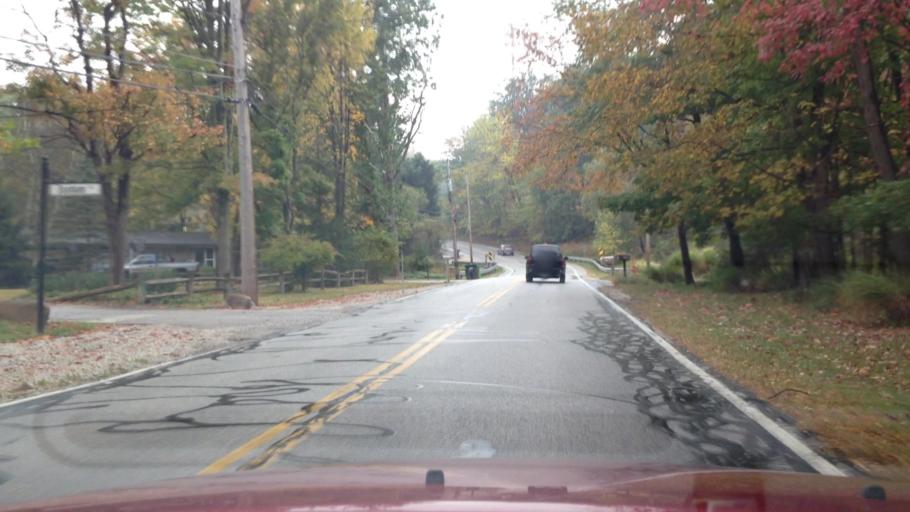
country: US
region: Ohio
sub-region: Cuyahoga County
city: Walton Hills
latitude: 41.3560
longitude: -81.5620
